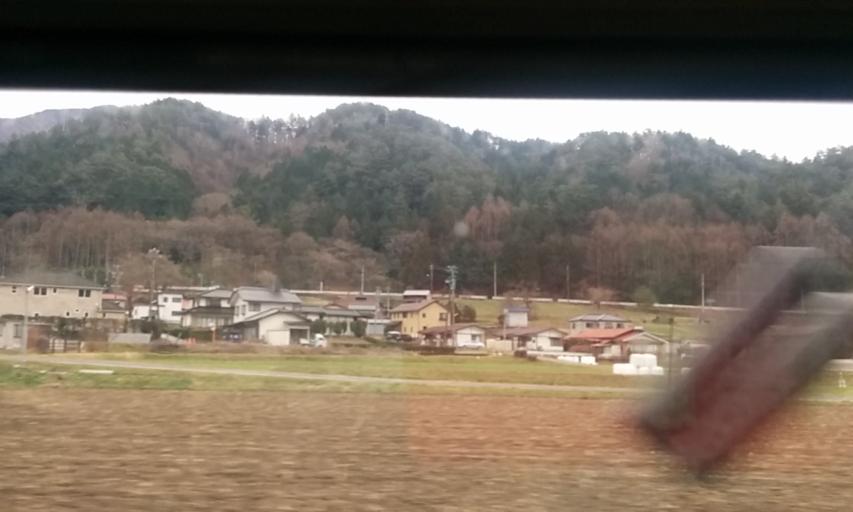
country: JP
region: Nagano
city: Ina
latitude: 35.8762
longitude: 137.7500
